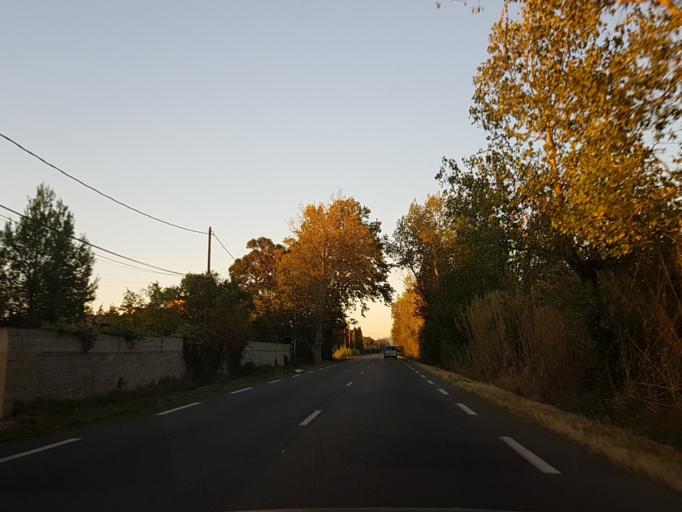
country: FR
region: Provence-Alpes-Cote d'Azur
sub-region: Departement du Vaucluse
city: Pernes-les-Fontaines
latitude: 44.0118
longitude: 5.0269
